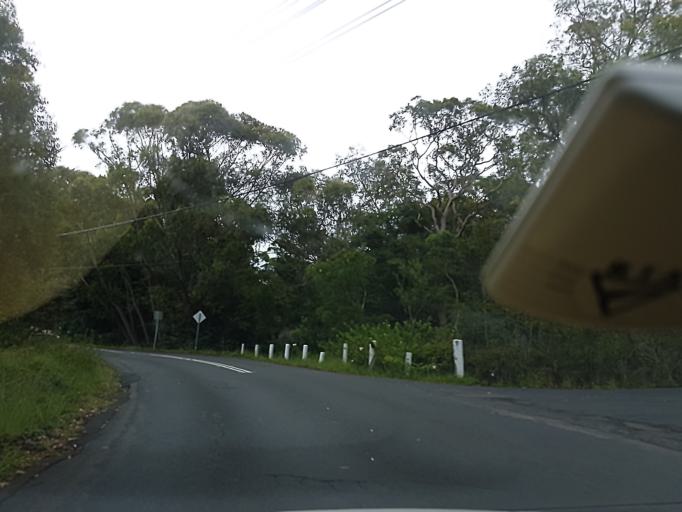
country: AU
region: New South Wales
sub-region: Warringah
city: Davidson
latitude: -33.7197
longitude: 151.2235
